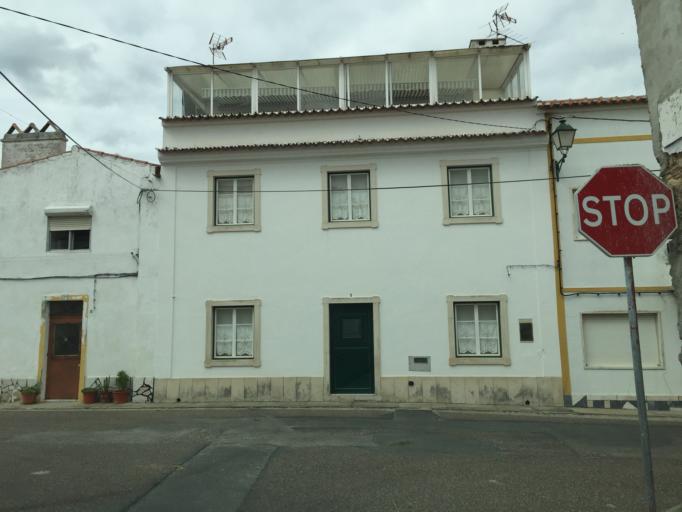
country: PT
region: Portalegre
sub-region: Ponte de Sor
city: Santo Andre
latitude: 39.0785
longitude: -8.1682
